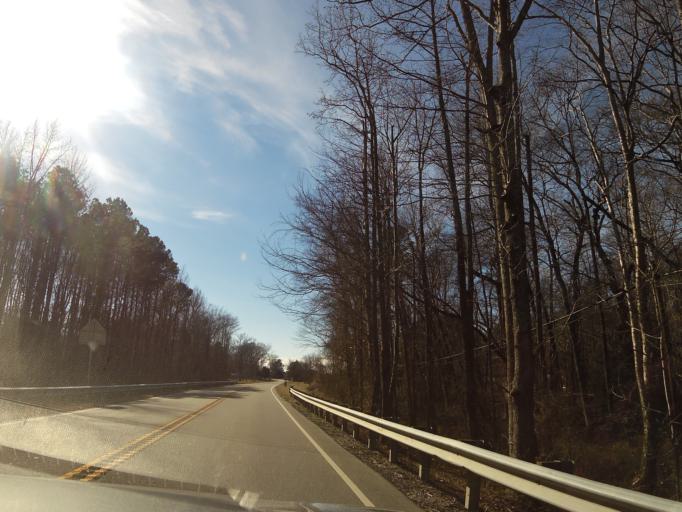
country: US
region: Virginia
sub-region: Isle of Wight County
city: Isle of Wight
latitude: 36.9067
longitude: -76.7094
